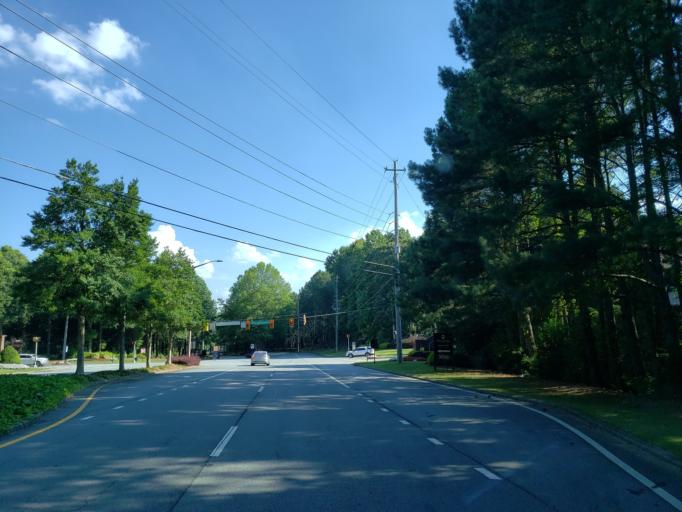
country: US
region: Georgia
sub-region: Cherokee County
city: Woodstock
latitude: 34.1185
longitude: -84.5542
